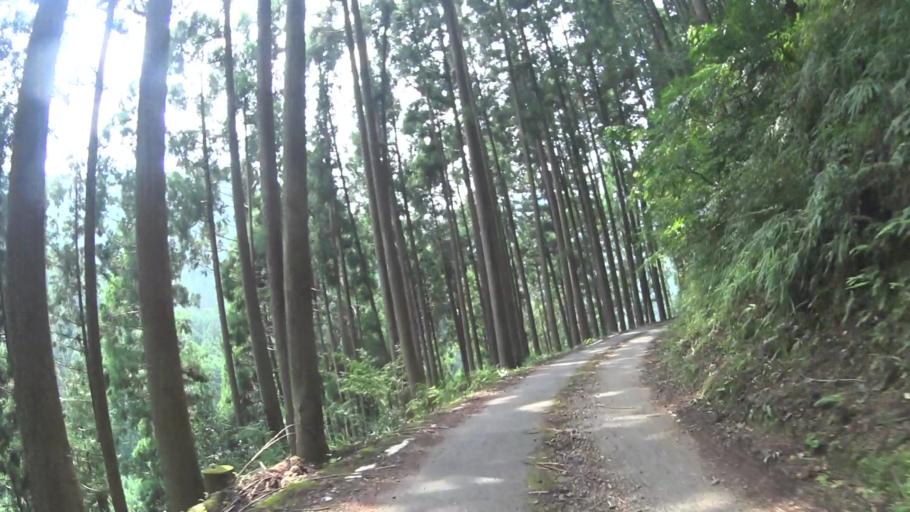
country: JP
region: Kyoto
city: Kameoka
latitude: 35.1984
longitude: 135.5860
